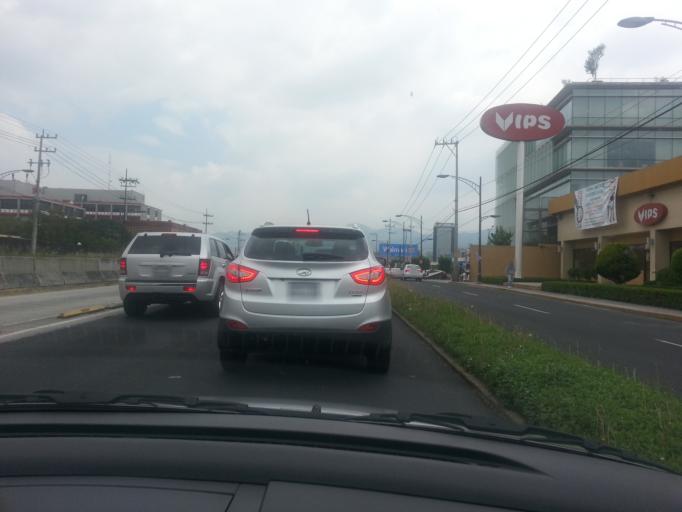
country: MX
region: Mexico City
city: Tlalpan
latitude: 19.3082
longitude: -99.1868
